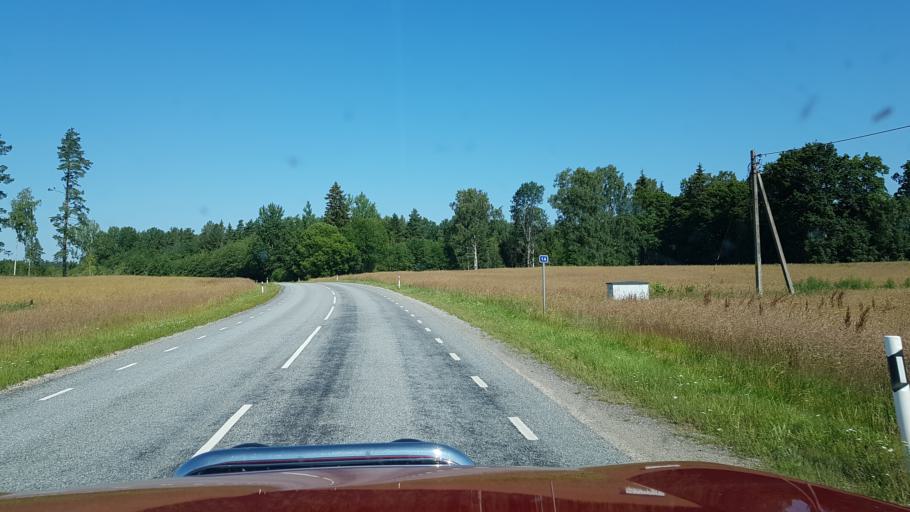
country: EE
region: Polvamaa
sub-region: Polva linn
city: Polva
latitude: 58.0849
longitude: 26.8328
